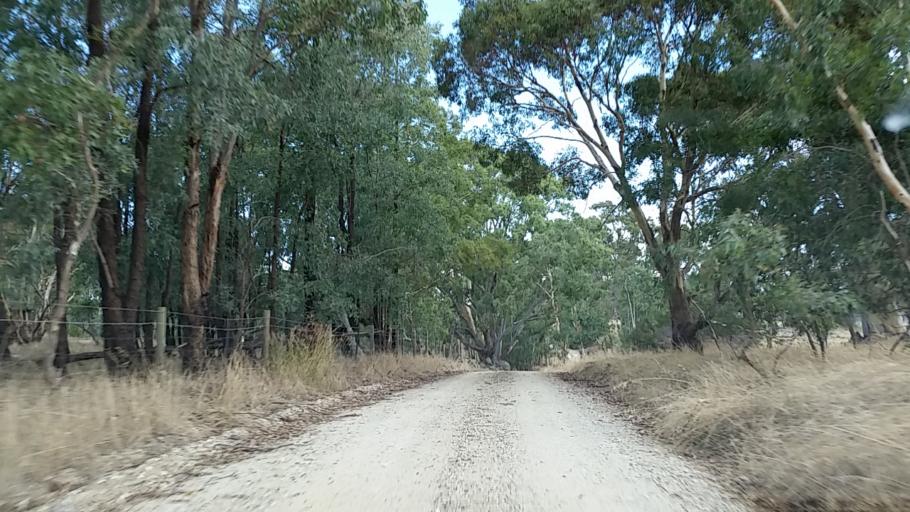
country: AU
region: South Australia
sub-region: Barossa
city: Angaston
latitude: -34.5684
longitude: 139.0743
